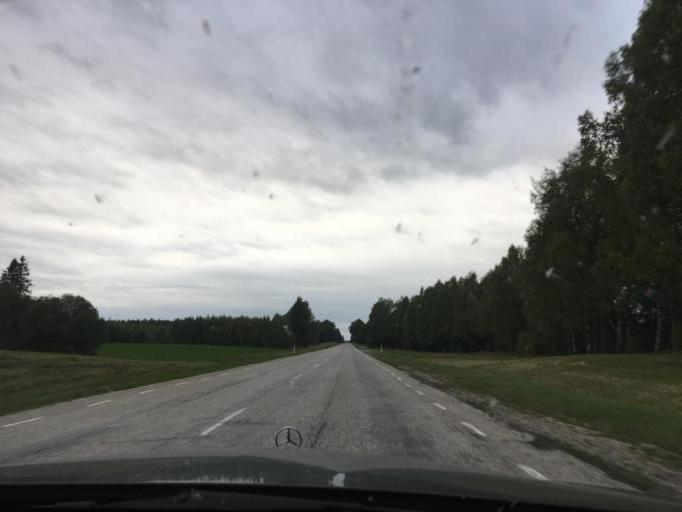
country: LV
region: Aluksnes Rajons
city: Aluksne
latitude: 57.5983
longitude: 27.1883
